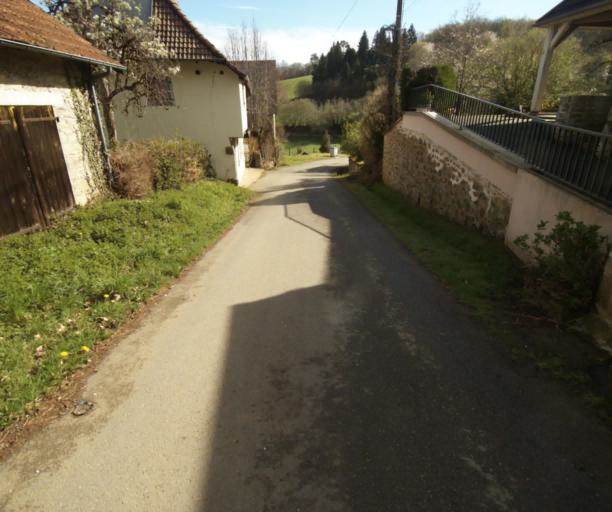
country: FR
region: Limousin
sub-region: Departement de la Correze
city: Laguenne
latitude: 45.2616
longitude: 1.8210
